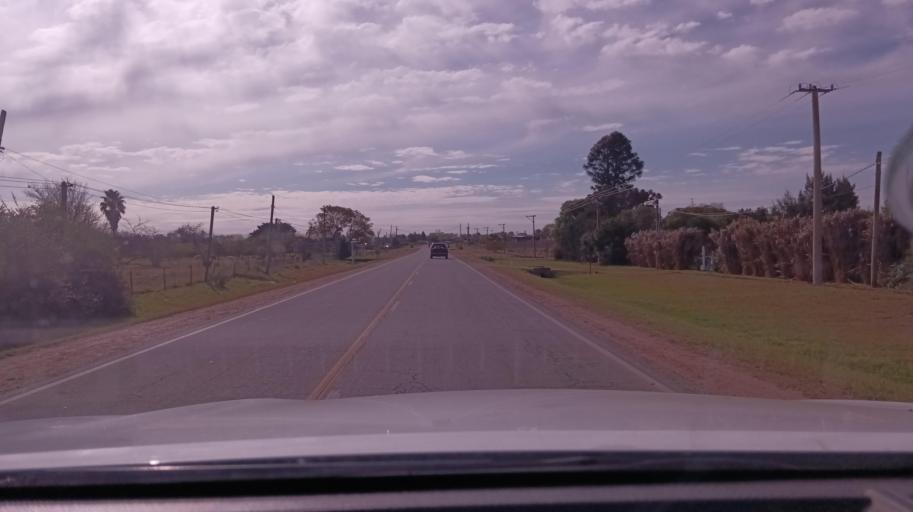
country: UY
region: Canelones
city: Toledo
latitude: -34.7200
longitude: -56.1132
